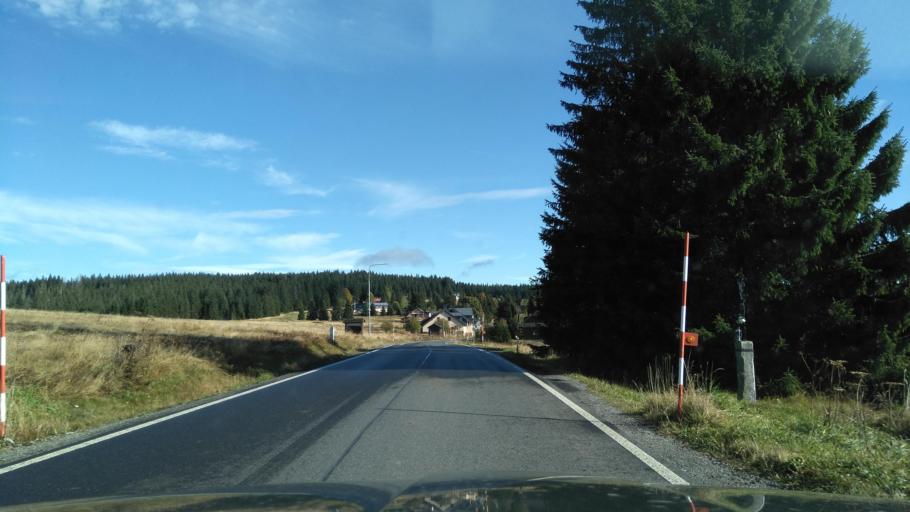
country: CZ
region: Plzensky
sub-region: Okres Klatovy
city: Kasperske Hory
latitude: 49.0269
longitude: 13.5154
